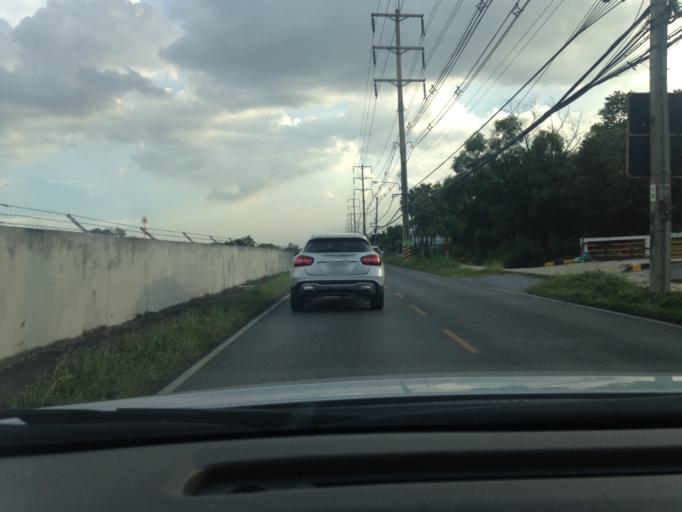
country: TH
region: Bangkok
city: Don Mueang
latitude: 13.9191
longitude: 100.5599
